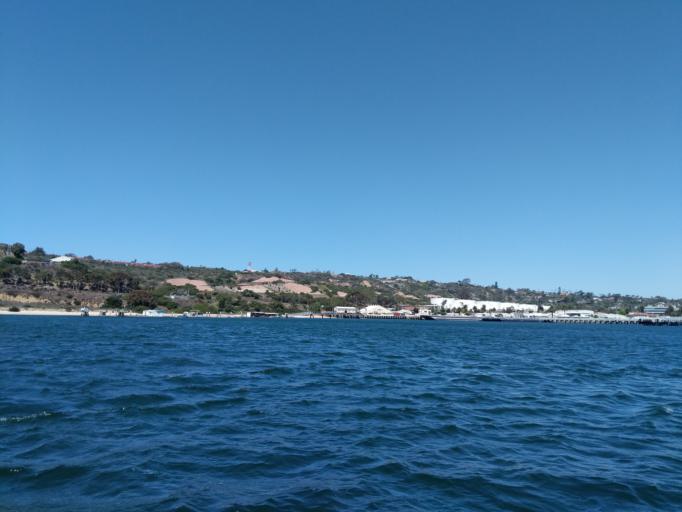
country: US
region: California
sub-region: San Diego County
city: Coronado
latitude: 32.6959
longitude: -117.2355
